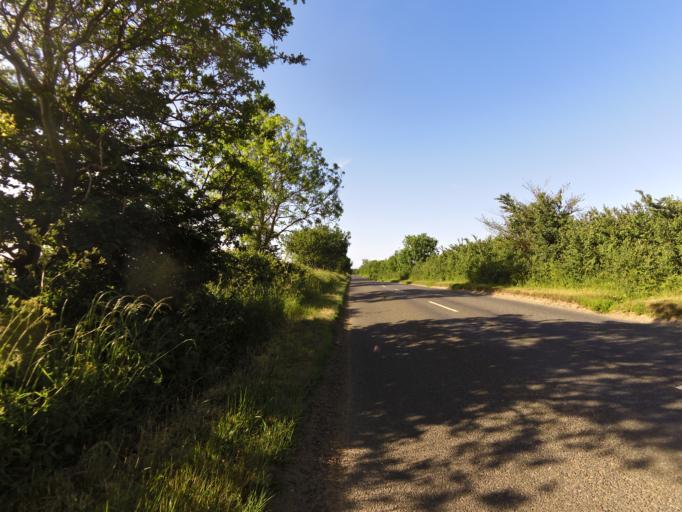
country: GB
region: England
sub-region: Suffolk
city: Woodbridge
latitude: 52.0723
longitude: 1.3629
